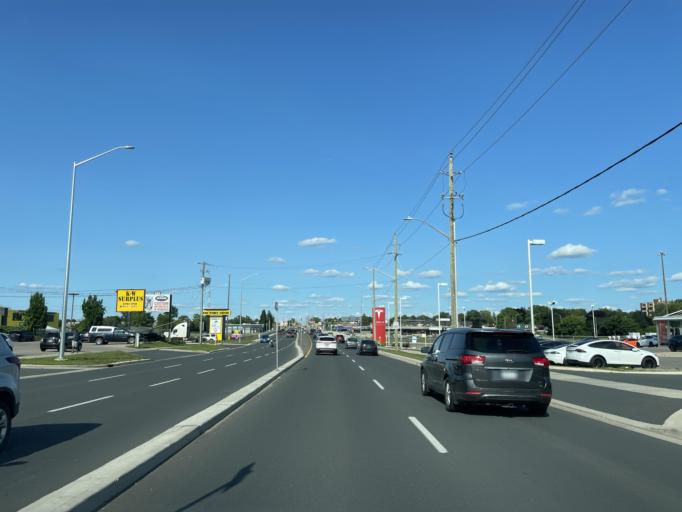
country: CA
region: Ontario
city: Waterloo
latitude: 43.4613
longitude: -80.4735
